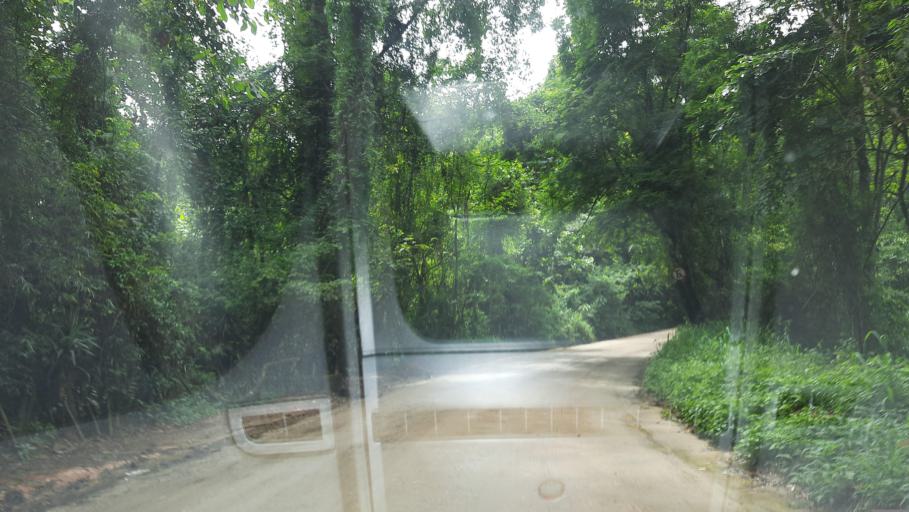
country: BR
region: Sao Paulo
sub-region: Franco Da Rocha
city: Franco da Rocha
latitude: -23.3294
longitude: -46.6731
